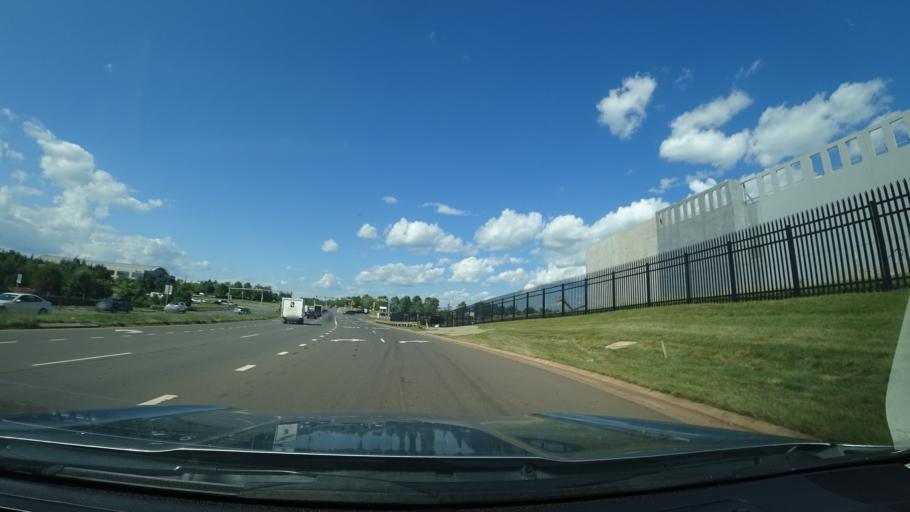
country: US
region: Virginia
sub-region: Loudoun County
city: Sterling
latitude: 39.0100
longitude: -77.4577
